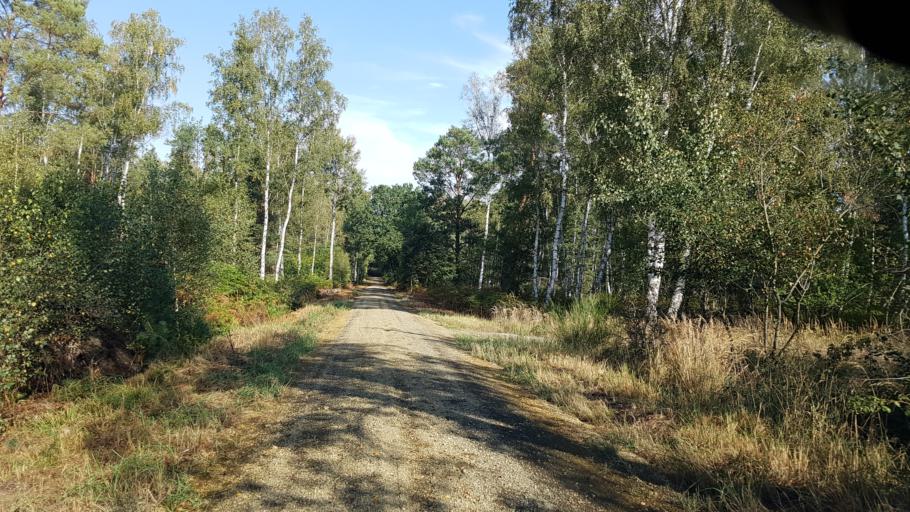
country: DE
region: Brandenburg
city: Plessa
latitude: 51.5151
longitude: 13.6404
